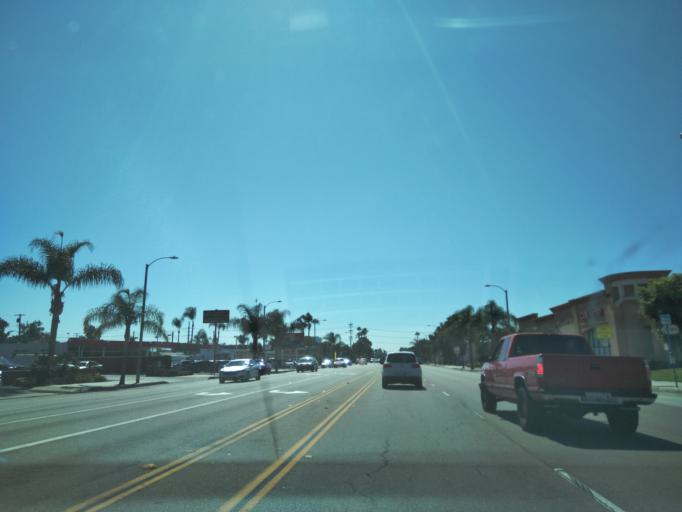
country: US
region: California
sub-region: Orange County
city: Santa Ana
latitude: 33.7157
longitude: -117.8681
